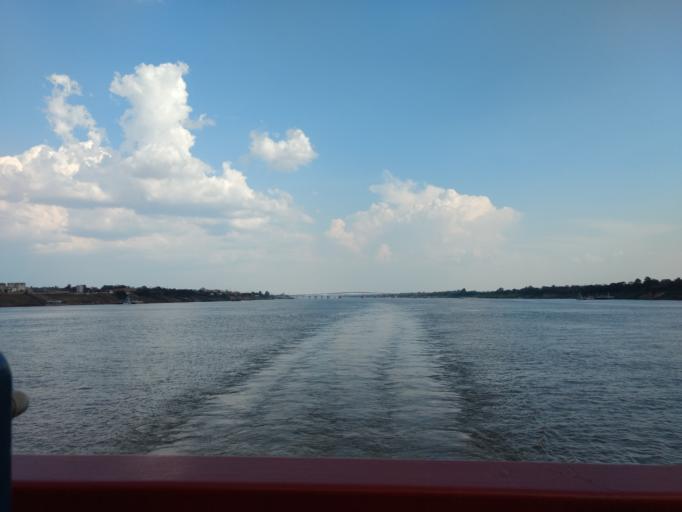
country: BR
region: Rondonia
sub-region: Porto Velho
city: Porto Velho
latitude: -8.7029
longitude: -63.9228
